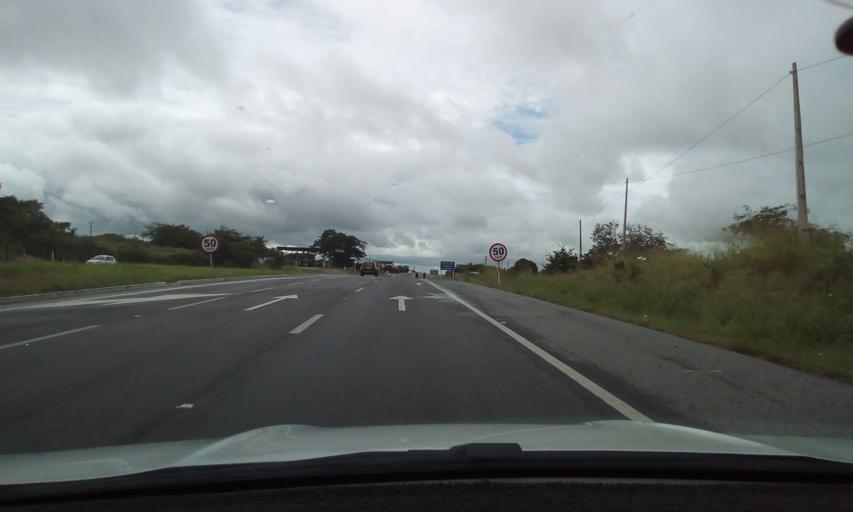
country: BR
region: Paraiba
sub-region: Gurinhem
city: Gurinhem
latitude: -7.1739
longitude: -35.3974
